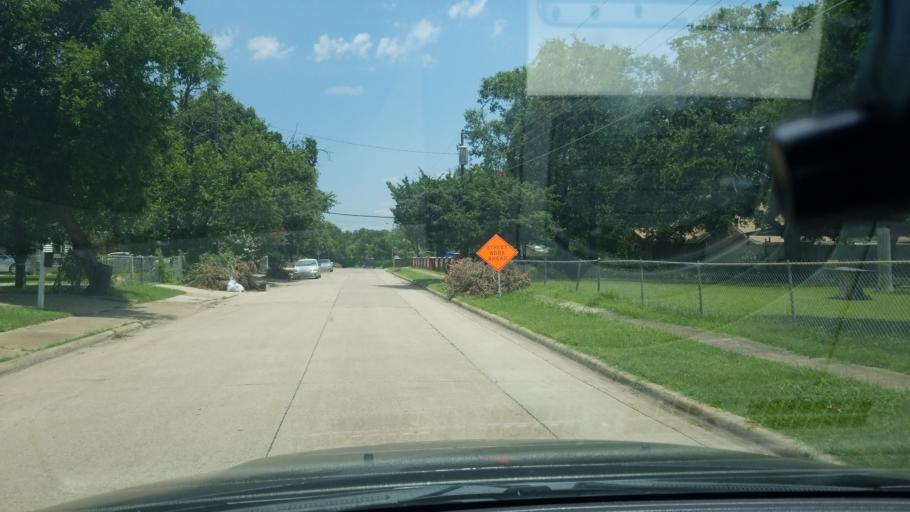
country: US
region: Texas
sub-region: Dallas County
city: Balch Springs
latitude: 32.7242
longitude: -96.6692
